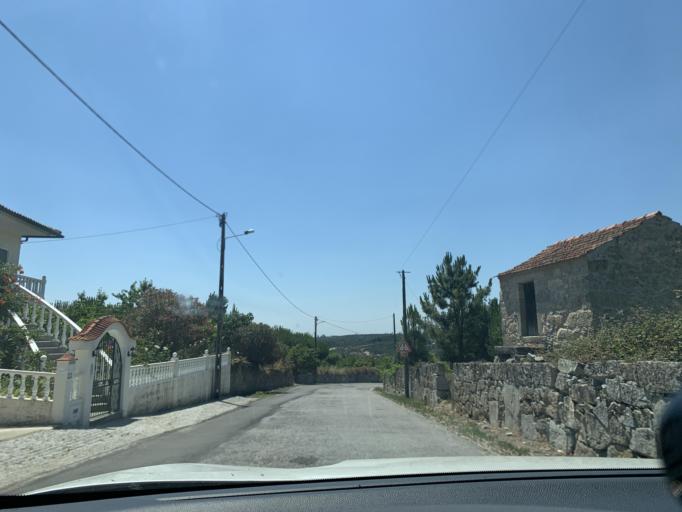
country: PT
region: Viseu
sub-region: Mangualde
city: Mangualde
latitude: 40.5558
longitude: -7.7276
